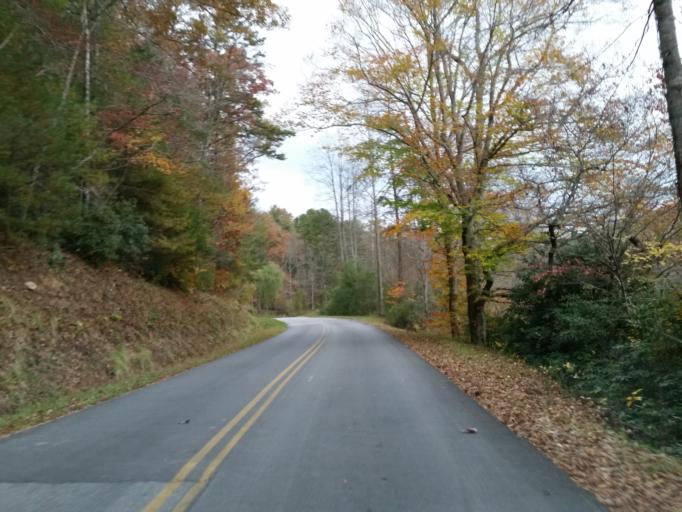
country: US
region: Georgia
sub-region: Fannin County
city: Blue Ridge
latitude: 34.7578
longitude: -84.1873
